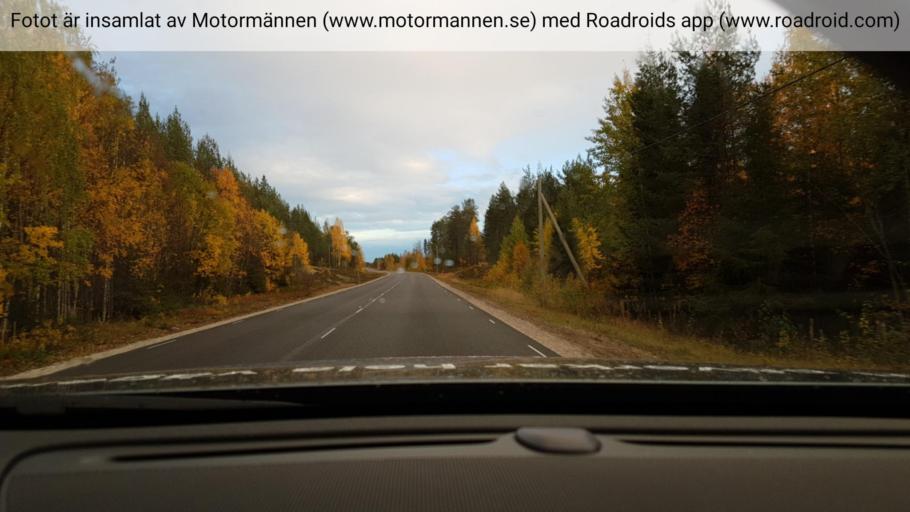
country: SE
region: Norrbotten
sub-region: Overkalix Kommun
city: OEverkalix
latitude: 66.3870
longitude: 22.8243
